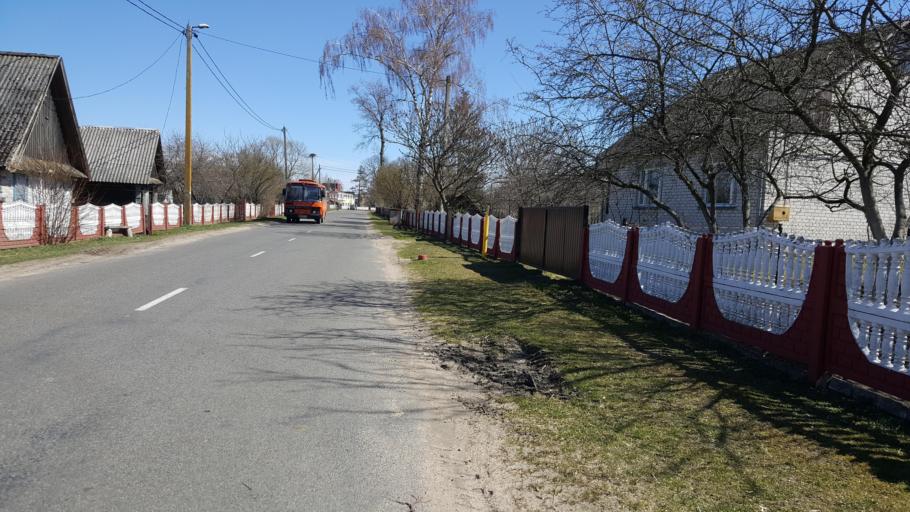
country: BY
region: Brest
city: Zhabinka
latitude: 52.2527
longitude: 23.9031
